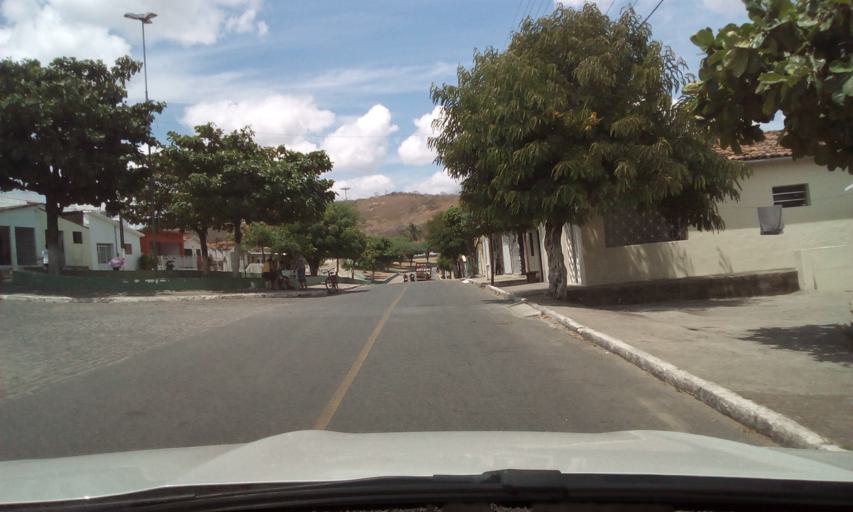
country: BR
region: Paraiba
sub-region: Gurinhem
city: Gurinhem
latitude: -7.1239
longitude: -35.4255
